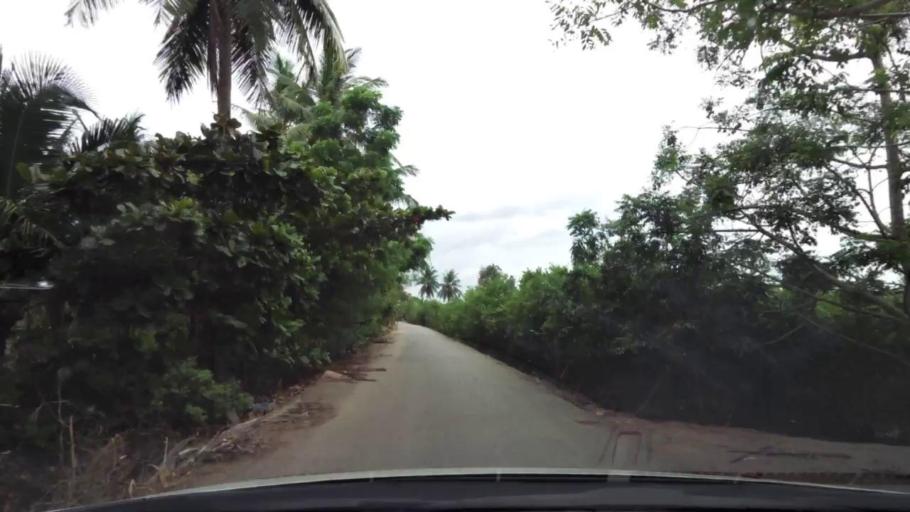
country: TH
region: Ratchaburi
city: Damnoen Saduak
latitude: 13.5705
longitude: 100.0034
